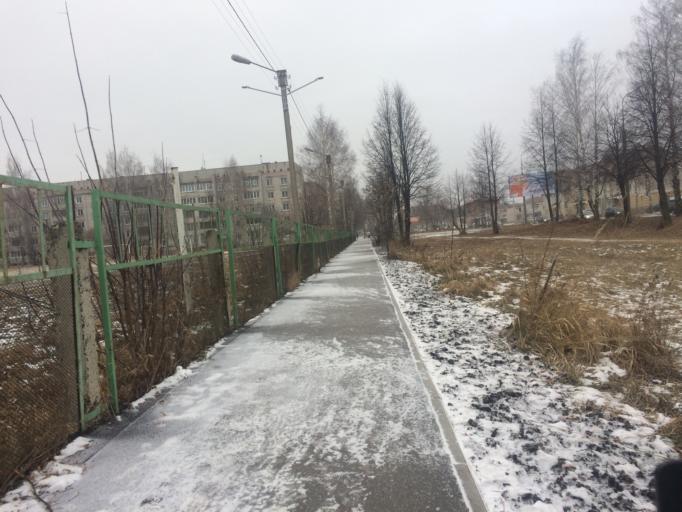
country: RU
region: Mariy-El
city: Yoshkar-Ola
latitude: 56.6535
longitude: 47.8700
